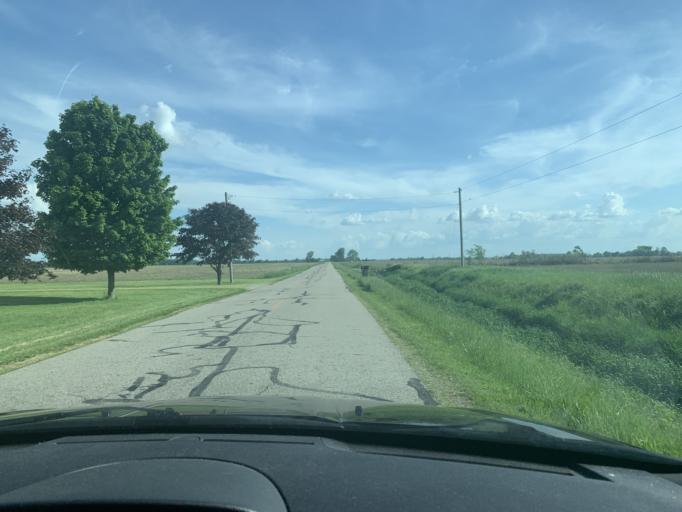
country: US
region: Ohio
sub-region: Logan County
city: De Graff
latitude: 40.2796
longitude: -84.0142
